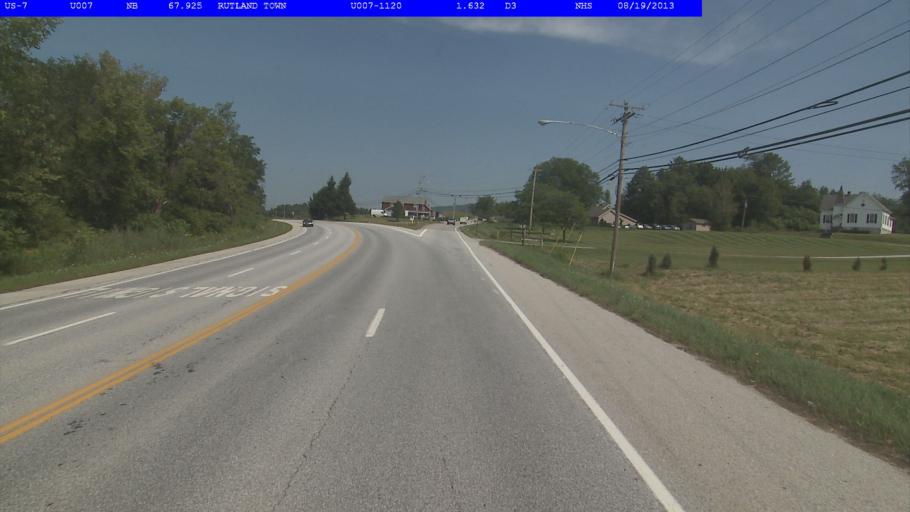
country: US
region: Vermont
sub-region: Rutland County
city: Rutland
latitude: 43.6367
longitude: -72.9756
